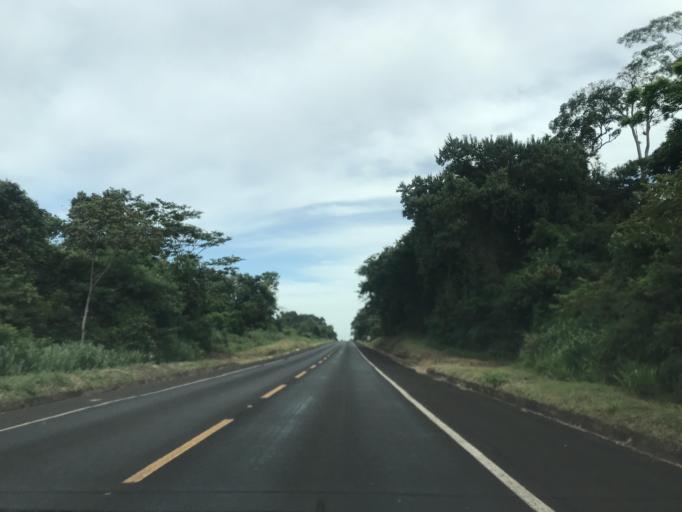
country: BR
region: Parana
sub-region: Paranavai
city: Paranavai
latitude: -23.0217
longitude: -52.4964
